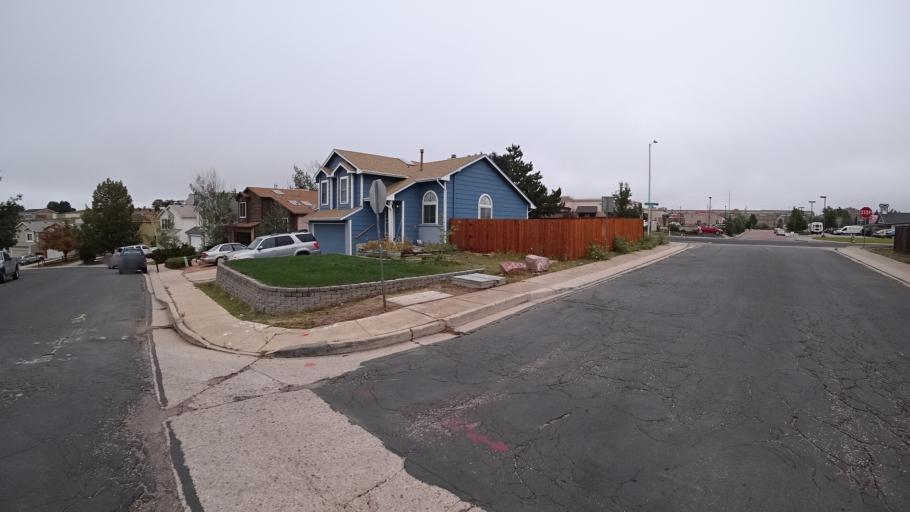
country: US
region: Colorado
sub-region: El Paso County
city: Black Forest
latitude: 38.9357
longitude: -104.7589
